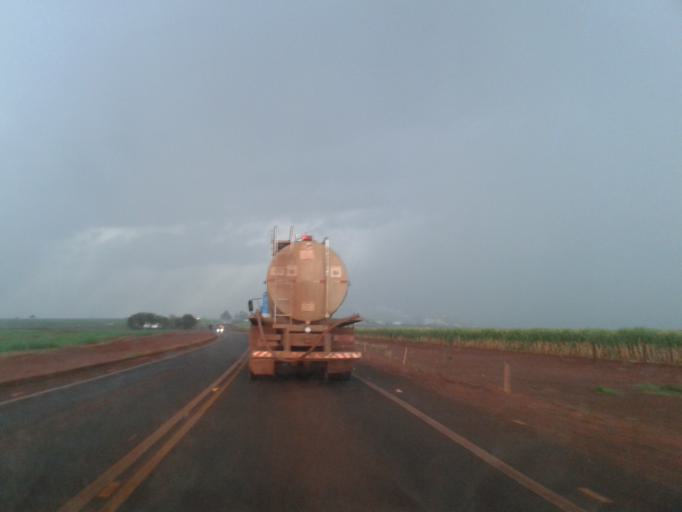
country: BR
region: Goias
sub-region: Quirinopolis
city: Quirinopolis
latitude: -18.5667
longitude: -50.4379
